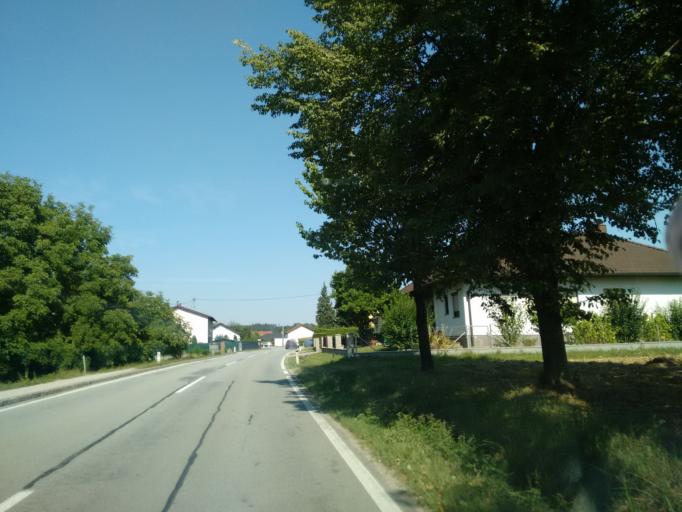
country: AT
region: Upper Austria
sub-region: Politischer Bezirk Grieskirchen
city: Bad Schallerbach
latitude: 48.1926
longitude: 13.9188
